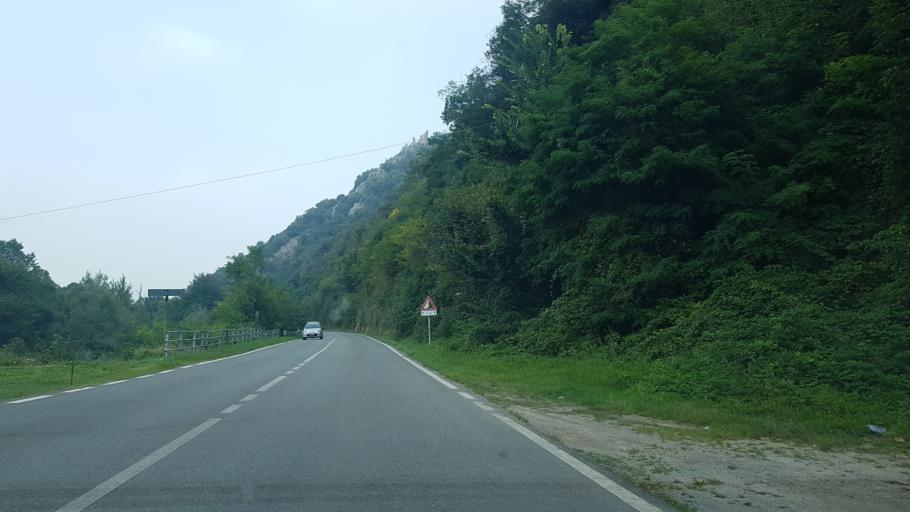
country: IT
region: Piedmont
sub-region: Provincia di Cuneo
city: Chiusa di Pesio
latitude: 44.3209
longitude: 7.6842
